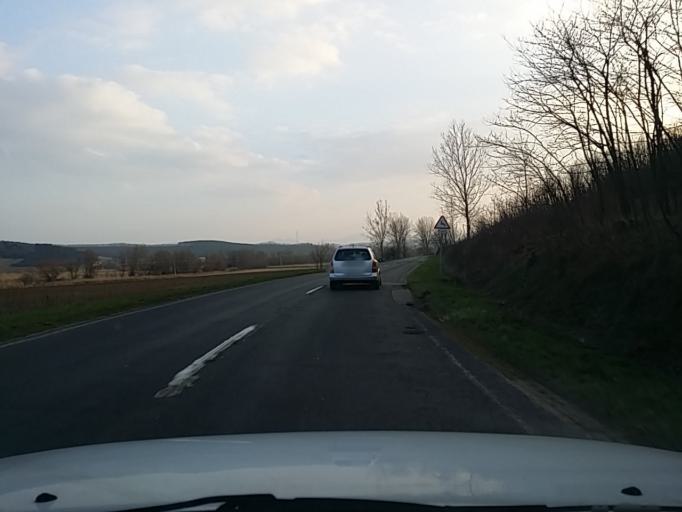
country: HU
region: Heves
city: Petervasara
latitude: 48.0400
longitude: 20.1271
